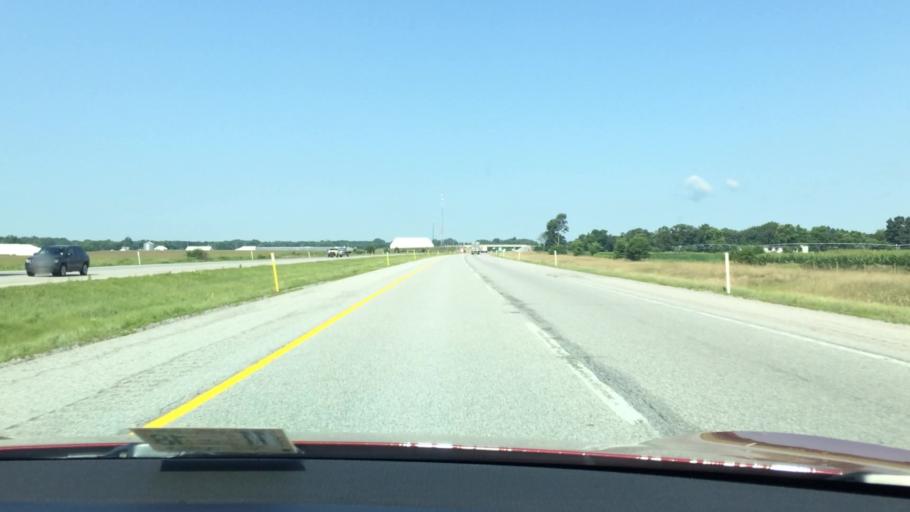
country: US
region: Michigan
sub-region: Saint Joseph County
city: White Pigeon
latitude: 41.7455
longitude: -85.5321
